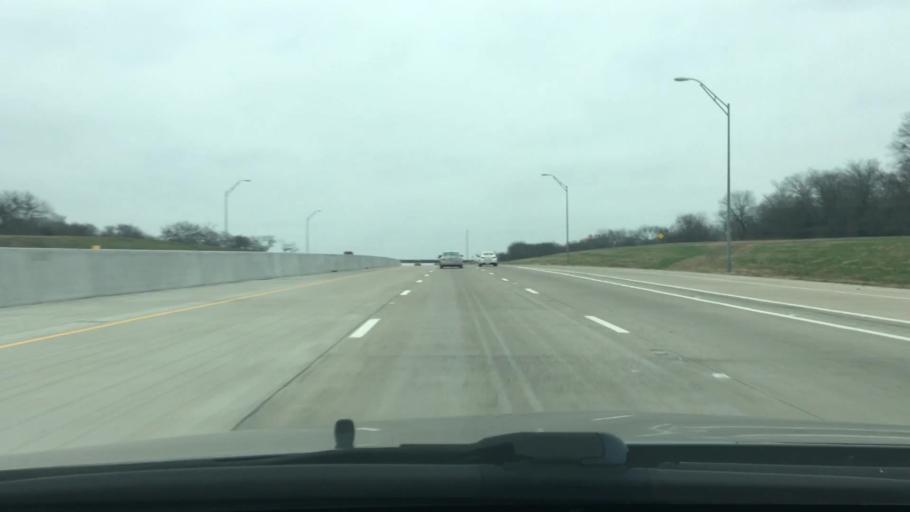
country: US
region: Texas
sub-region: Freestone County
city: Wortham
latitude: 31.9068
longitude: -96.3874
